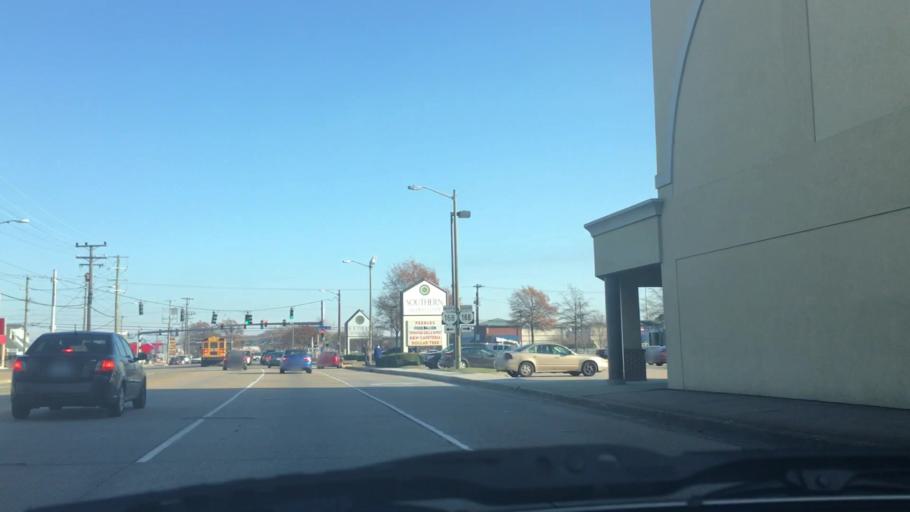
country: US
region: Virginia
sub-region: City of Norfolk
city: Norfolk
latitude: 36.9166
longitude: -76.2557
